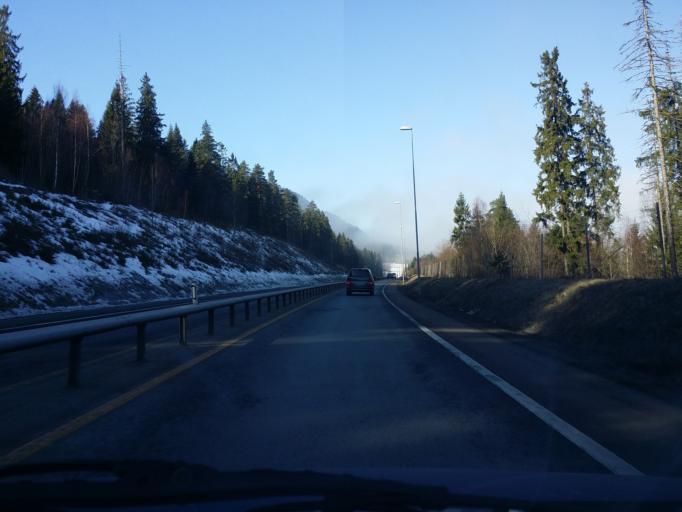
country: NO
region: Buskerud
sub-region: Nedre Eiker
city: Mjondalen
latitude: 59.7421
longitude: 10.0852
